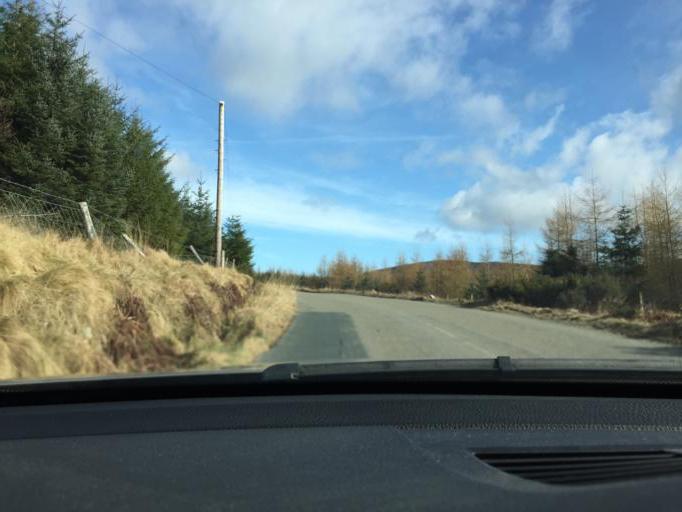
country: IE
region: Leinster
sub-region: Wicklow
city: Valleymount
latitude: 53.0603
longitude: -6.4526
